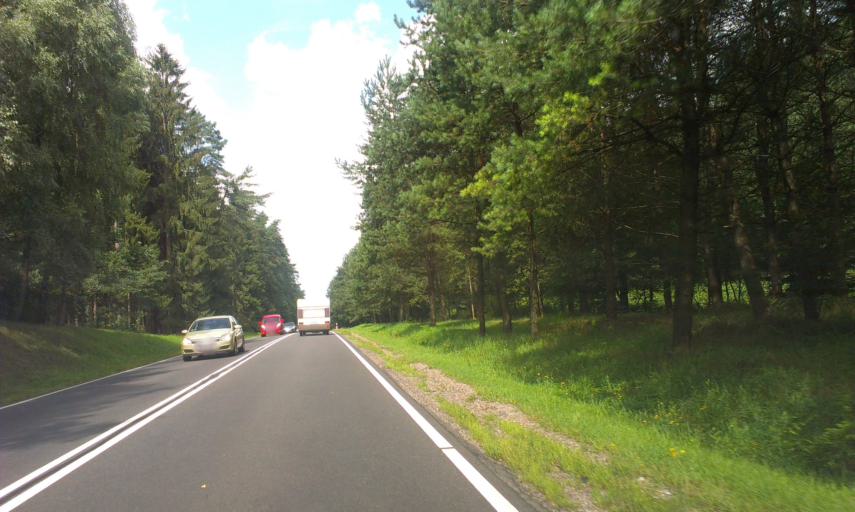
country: PL
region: West Pomeranian Voivodeship
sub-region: Powiat koszalinski
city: Sianow
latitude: 54.0841
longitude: 16.3817
